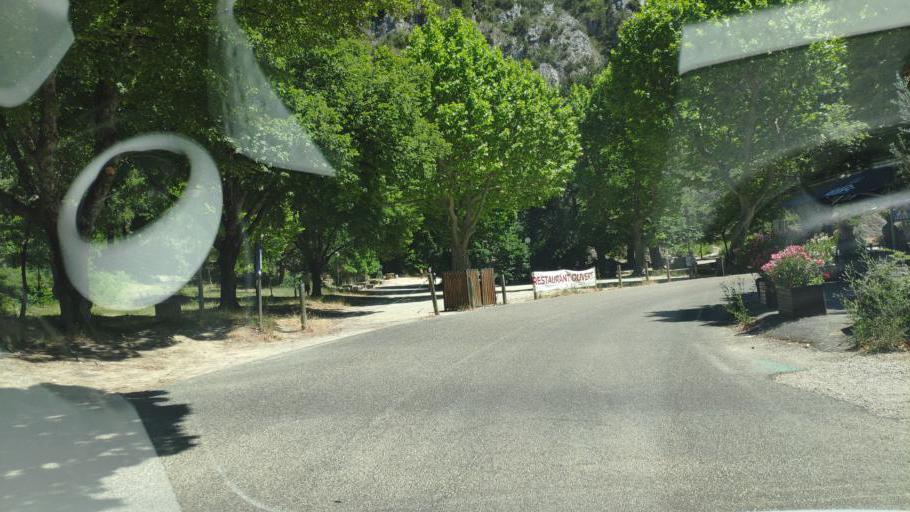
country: FR
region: Provence-Alpes-Cote d'Azur
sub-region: Departement du Vaucluse
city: Malaucene
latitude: 44.1672
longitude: 5.1485
